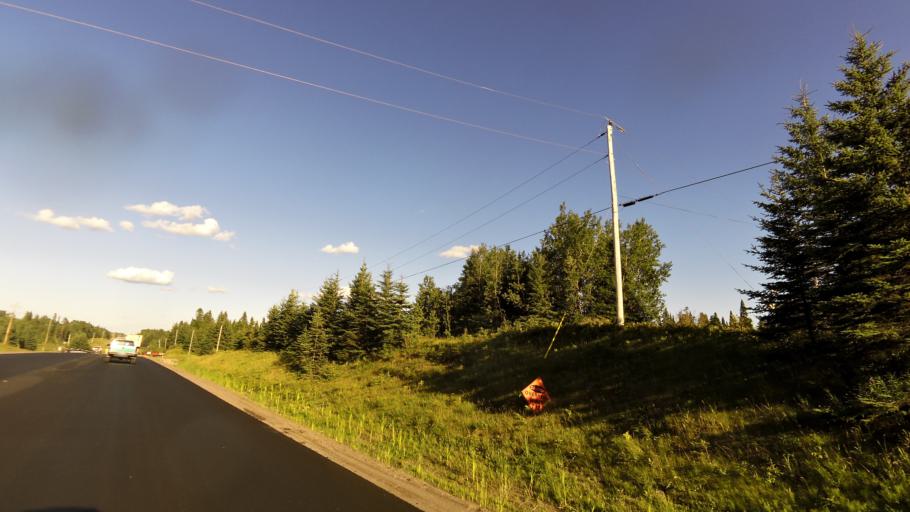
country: CA
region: Ontario
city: Dryden
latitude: 49.8151
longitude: -92.8805
